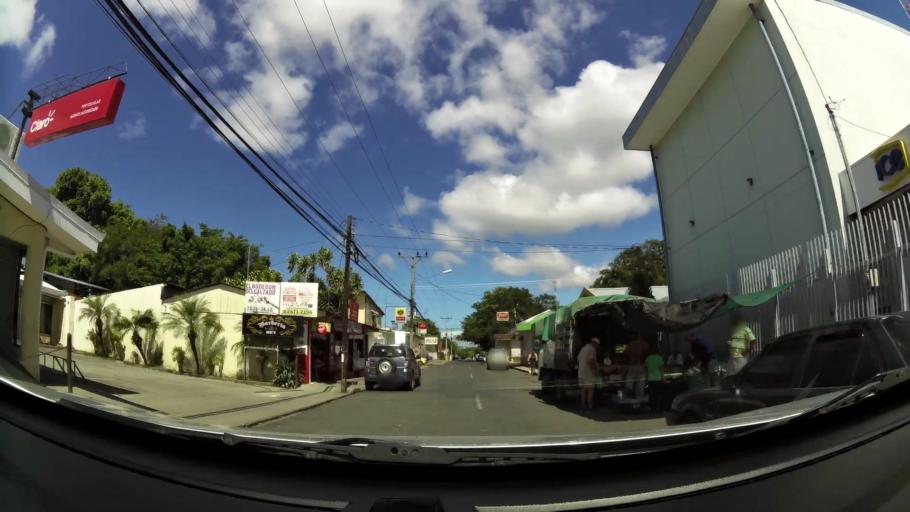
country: CR
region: Guanacaste
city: Bagaces
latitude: 10.5277
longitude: -85.2550
